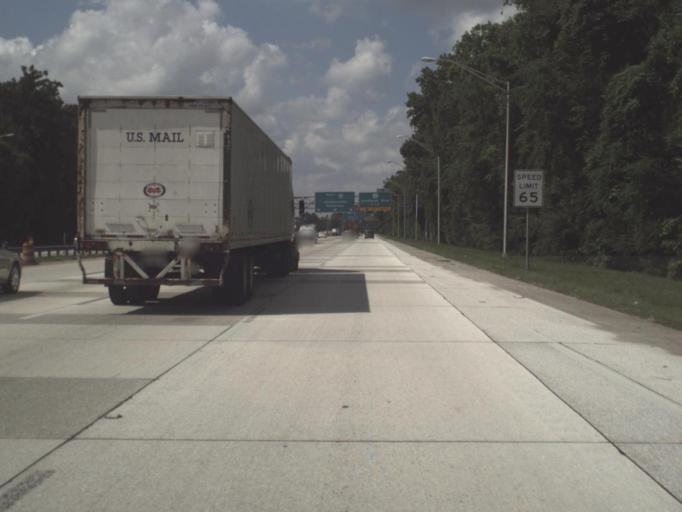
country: US
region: Florida
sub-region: Saint Johns County
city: Fruit Cove
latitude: 30.1903
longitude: -81.5569
